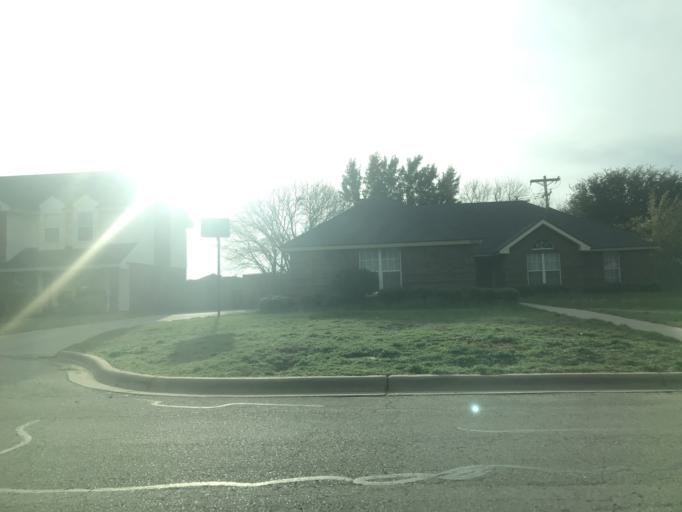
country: US
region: Texas
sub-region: Taylor County
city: Abilene
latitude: 32.3954
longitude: -99.7732
